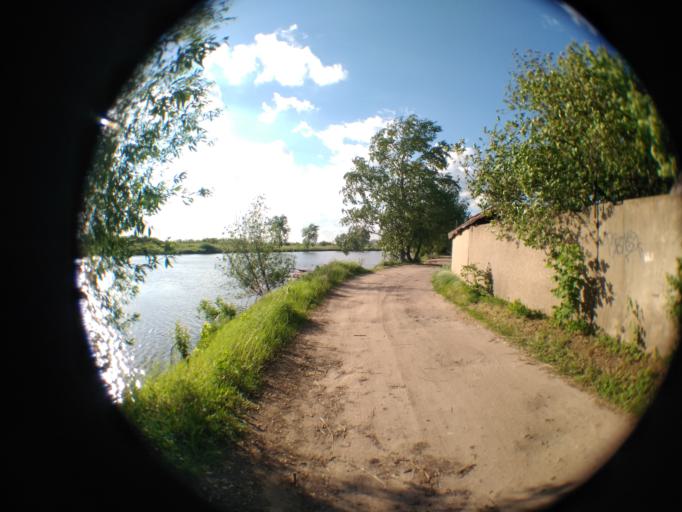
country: RU
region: Moskovskaya
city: Zhukovskiy
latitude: 55.5765
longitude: 38.1030
